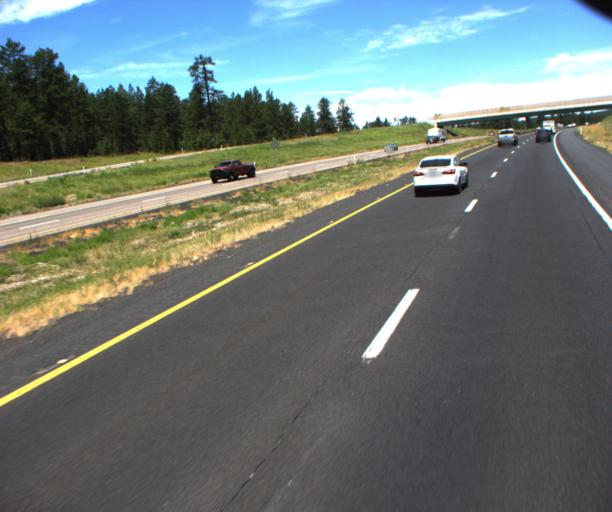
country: US
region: Arizona
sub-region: Coconino County
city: Sedona
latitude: 34.8734
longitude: -111.6336
